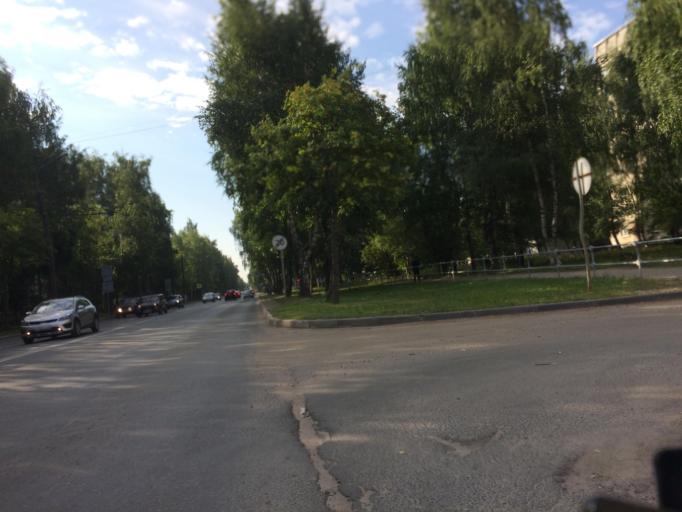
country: RU
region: Mariy-El
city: Medvedevo
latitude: 56.6387
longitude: 47.8325
